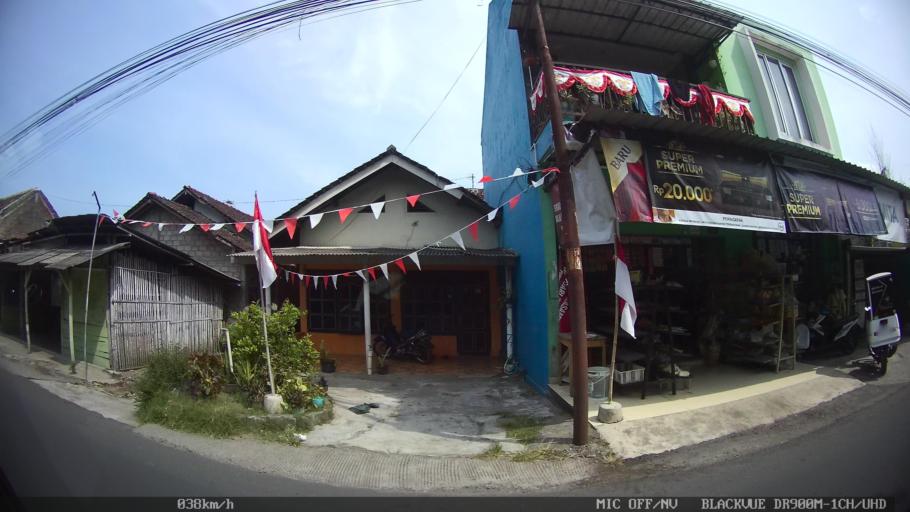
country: ID
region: Daerah Istimewa Yogyakarta
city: Depok
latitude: -7.8037
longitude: 110.4314
